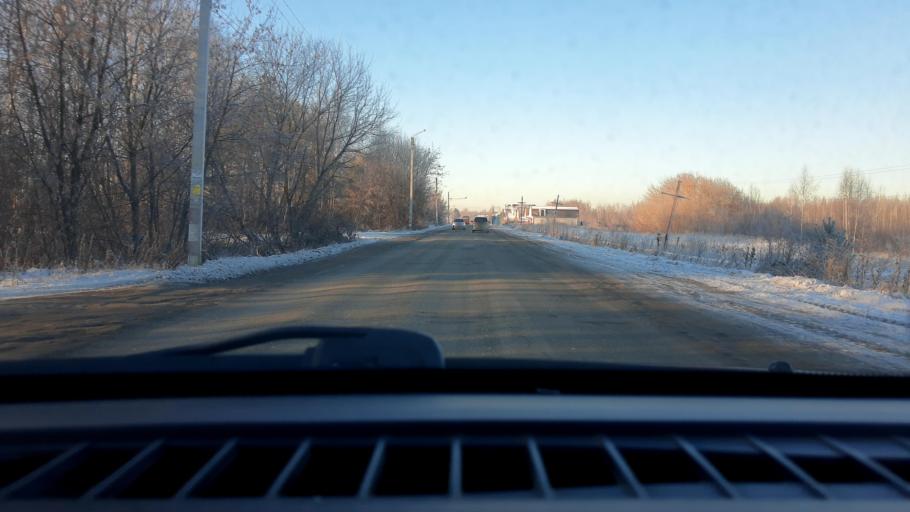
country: RU
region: Nizjnij Novgorod
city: Bor
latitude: 56.3690
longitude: 44.1106
